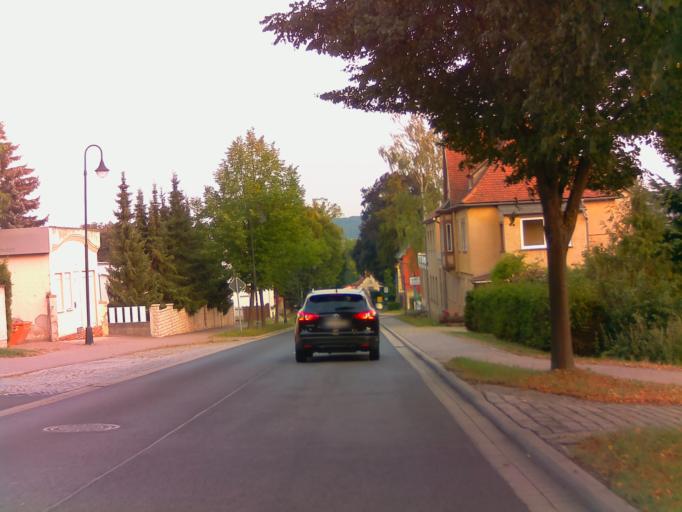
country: DE
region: Thuringia
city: Blankenhain
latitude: 50.8659
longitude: 11.3383
